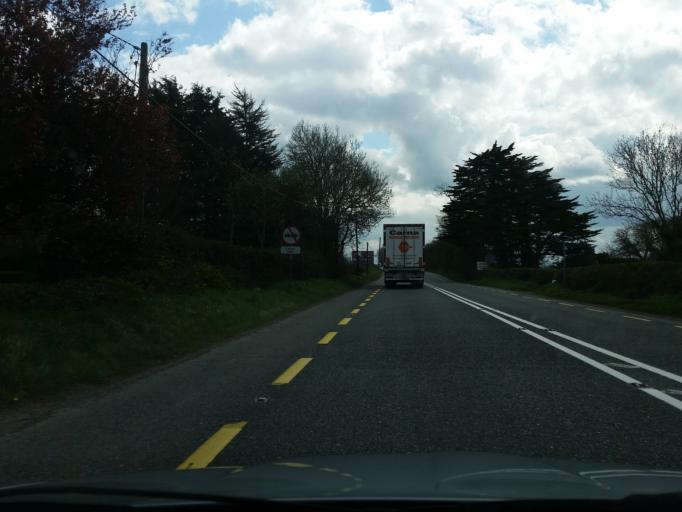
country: IE
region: Leinster
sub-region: An Mhi
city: Ratoath
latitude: 53.5511
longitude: -6.4349
